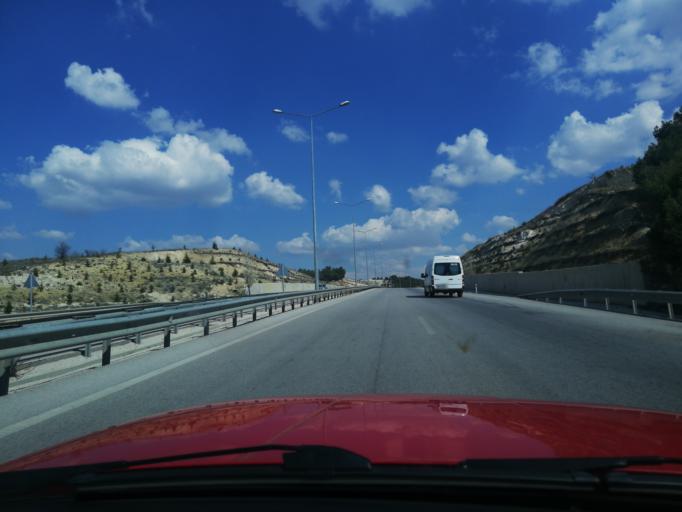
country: TR
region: Burdur
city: Burdur
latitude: 37.7011
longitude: 30.3133
